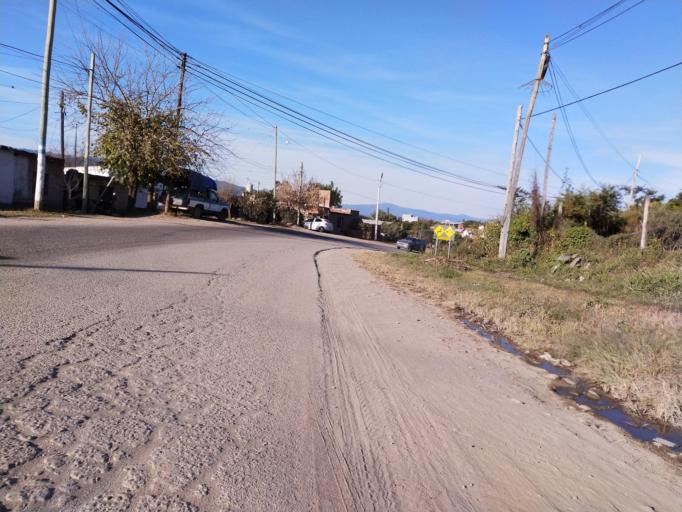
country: AR
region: Jujuy
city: San Salvador de Jujuy
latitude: -24.1790
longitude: -65.3437
